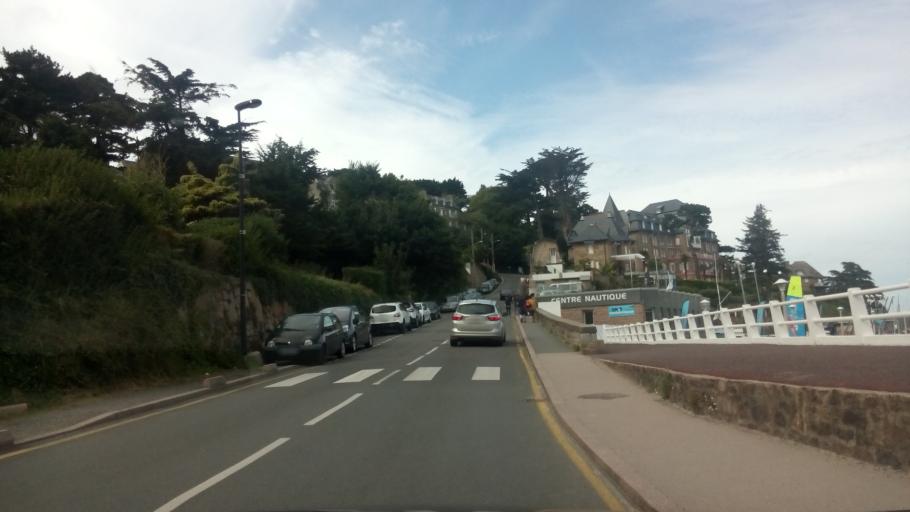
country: FR
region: Brittany
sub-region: Departement des Cotes-d'Armor
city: Perros-Guirec
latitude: 48.8171
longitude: -3.4609
